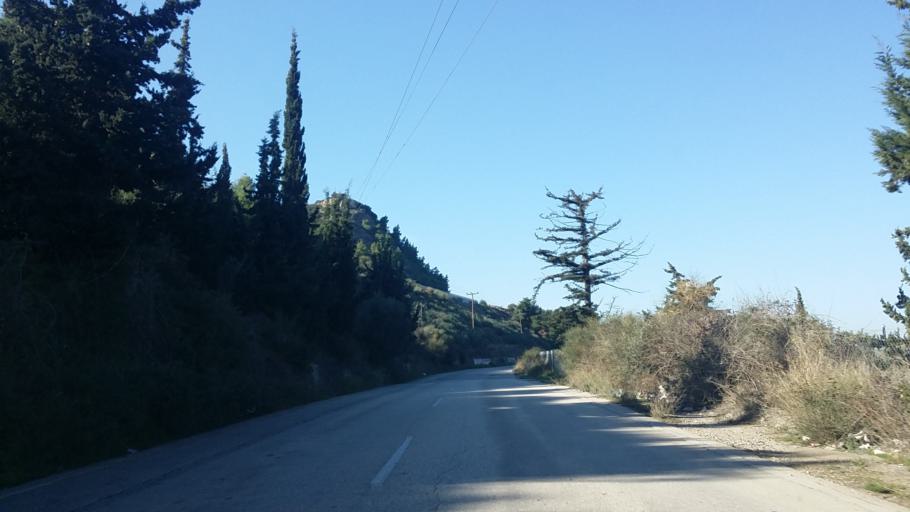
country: GR
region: West Greece
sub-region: Nomos Achaias
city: Akrata
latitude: 38.1793
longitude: 22.2178
